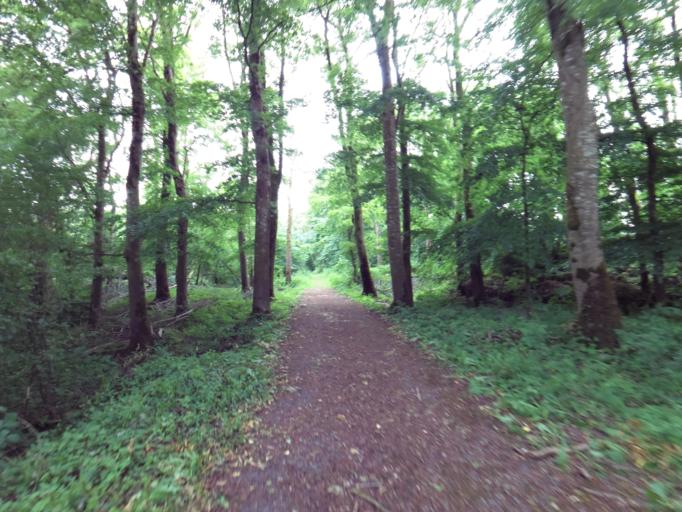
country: IE
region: Connaught
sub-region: County Galway
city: Gort
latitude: 53.0892
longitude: -8.8673
